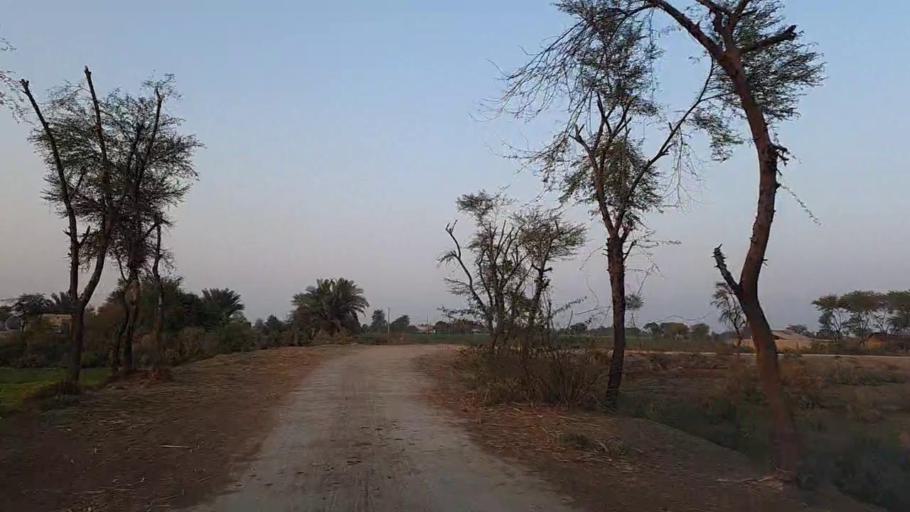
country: PK
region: Sindh
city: Jam Sahib
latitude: 26.3085
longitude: 68.5777
